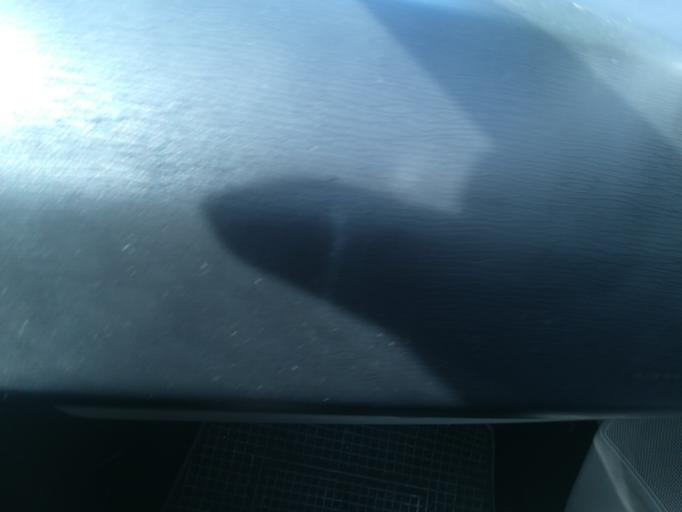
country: TR
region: Adana
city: Adana
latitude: 37.0318
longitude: 35.3227
